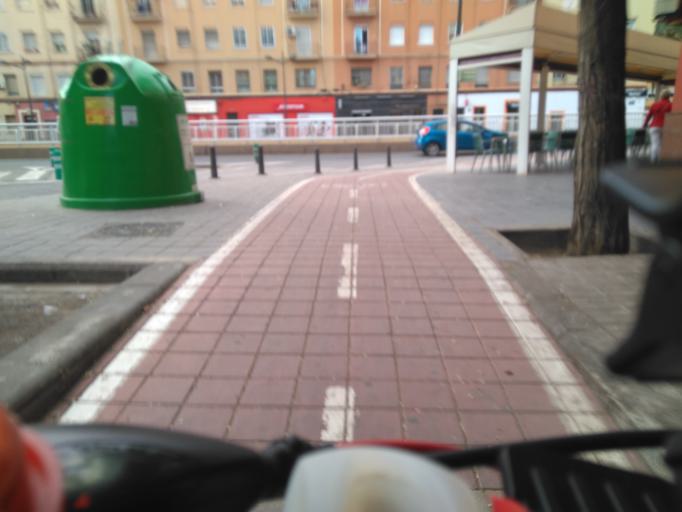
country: ES
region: Valencia
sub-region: Provincia de Valencia
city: Tavernes Blanques
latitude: 39.4900
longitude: -0.3854
